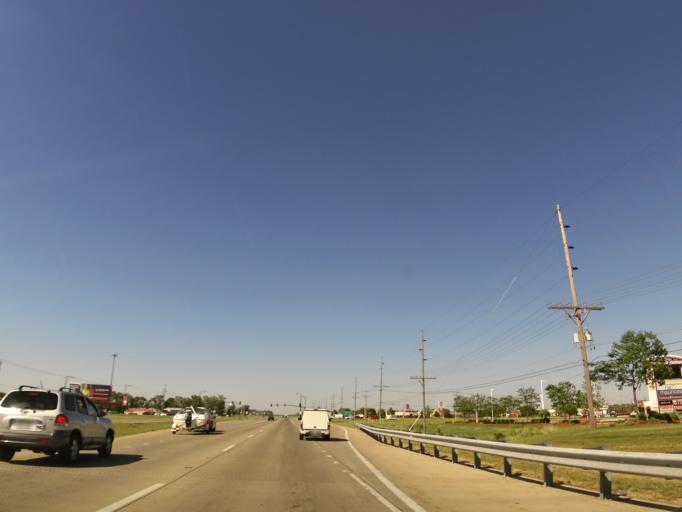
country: US
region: Illinois
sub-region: Winnebago County
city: Machesney Park
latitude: 42.3643
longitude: -89.0368
